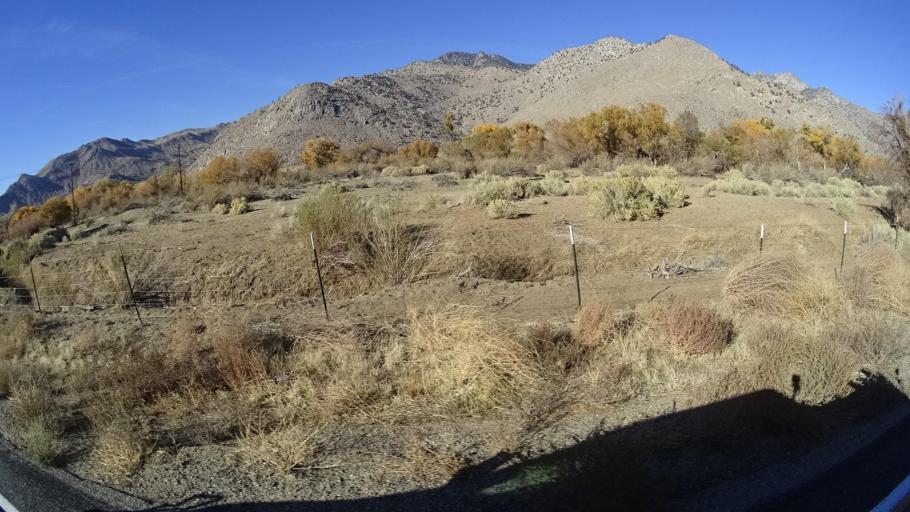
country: US
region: California
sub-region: Kern County
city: Weldon
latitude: 35.6856
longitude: -118.2411
